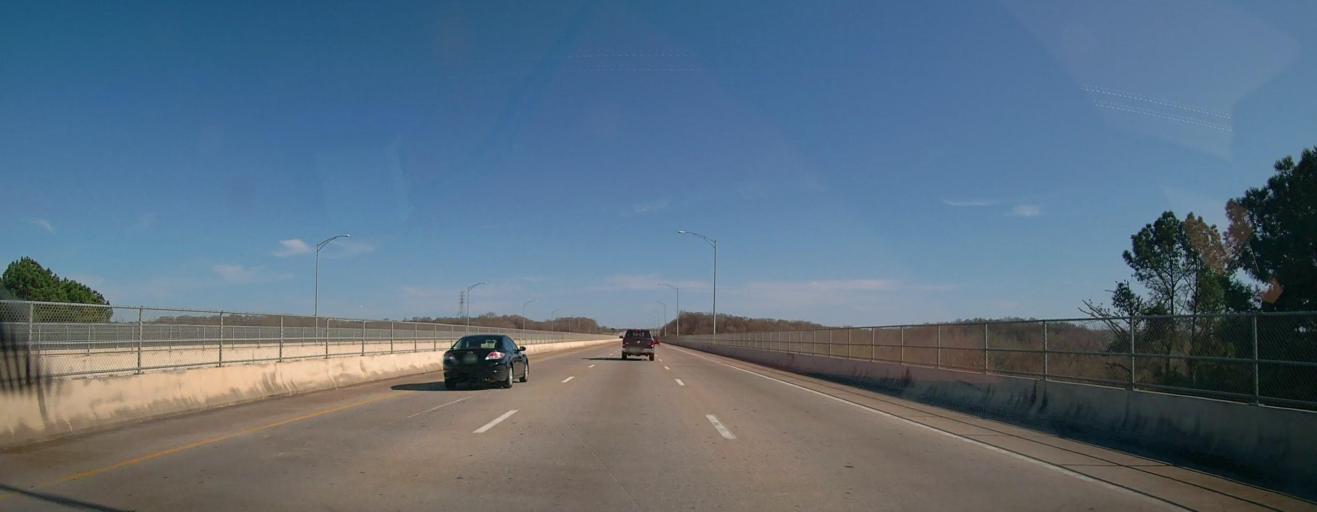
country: US
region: Alabama
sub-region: Lauderdale County
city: East Florence
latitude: 34.7971
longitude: -87.6475
